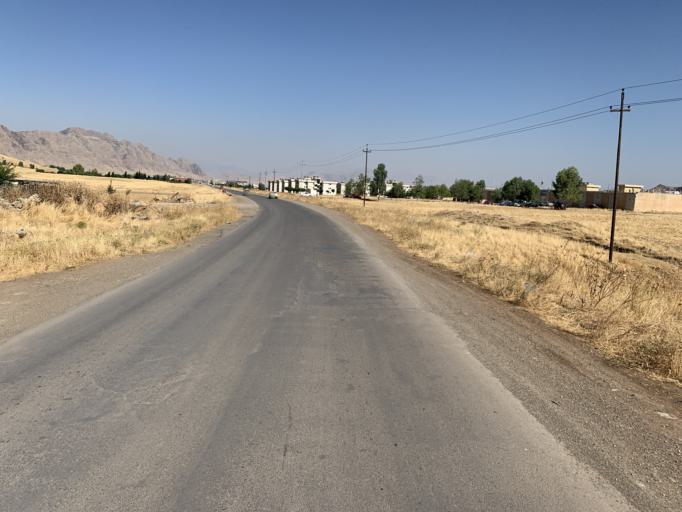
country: IQ
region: As Sulaymaniyah
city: Raniye
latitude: 36.2660
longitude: 44.8406
